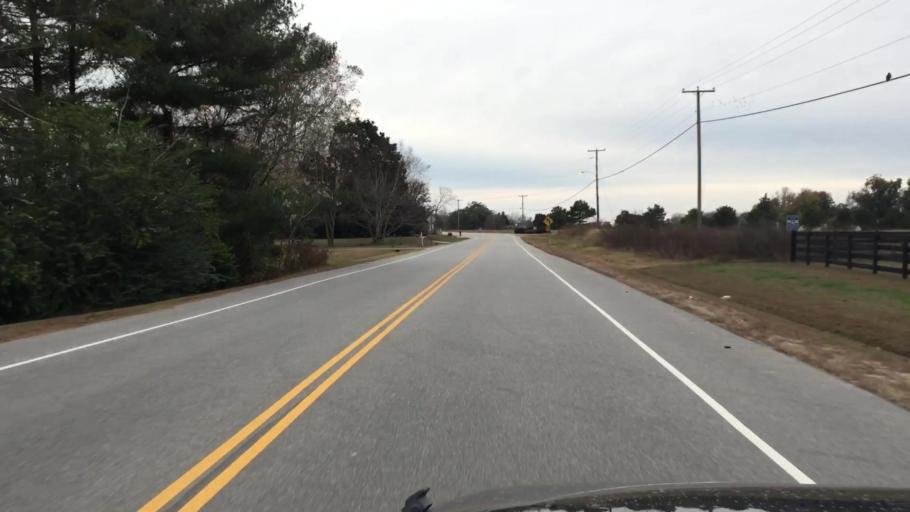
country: US
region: Virginia
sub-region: James City County
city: Williamsburg
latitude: 37.3825
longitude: -76.8101
